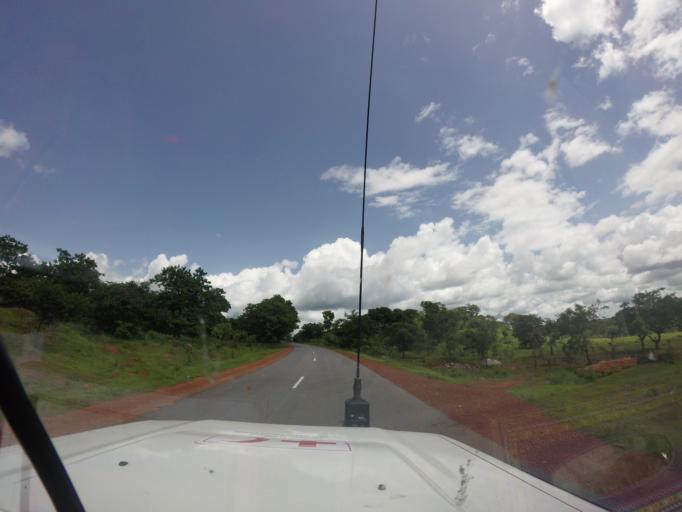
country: SL
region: Northern Province
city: Bindi
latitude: 10.1586
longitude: -11.4230
